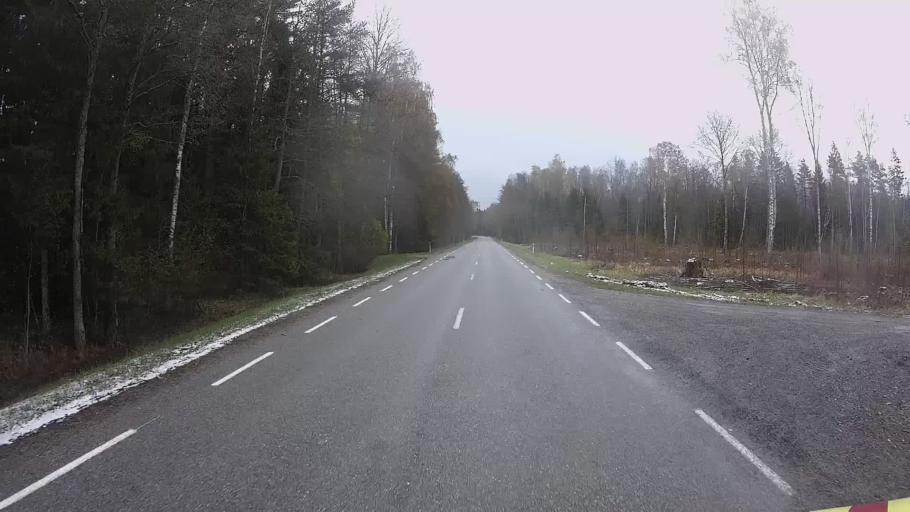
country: EE
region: Hiiumaa
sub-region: Kaerdla linn
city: Kardla
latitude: 59.0317
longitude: 22.6760
